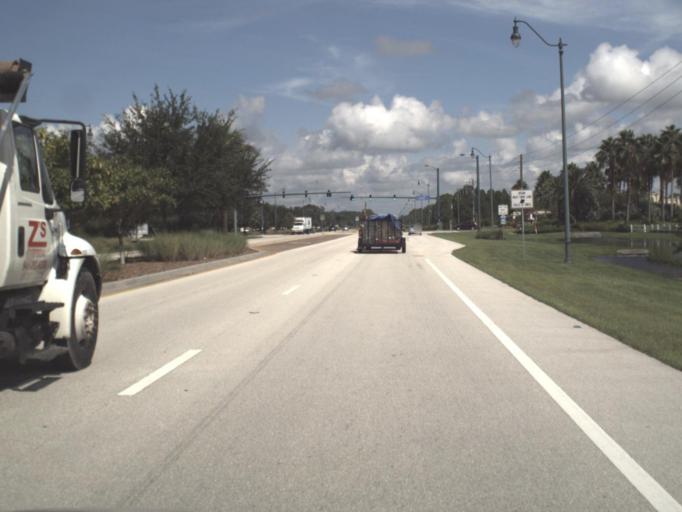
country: US
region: Florida
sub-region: Sarasota County
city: North Port
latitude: 27.0772
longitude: -82.1555
